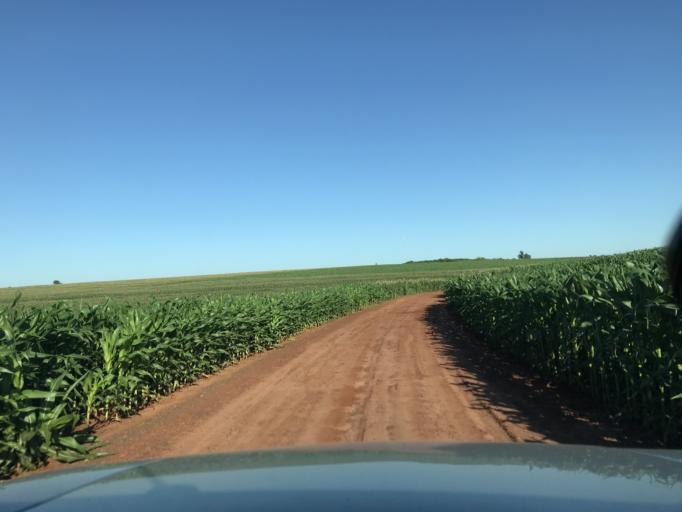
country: BR
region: Parana
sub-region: Palotina
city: Palotina
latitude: -24.2337
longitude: -53.7715
